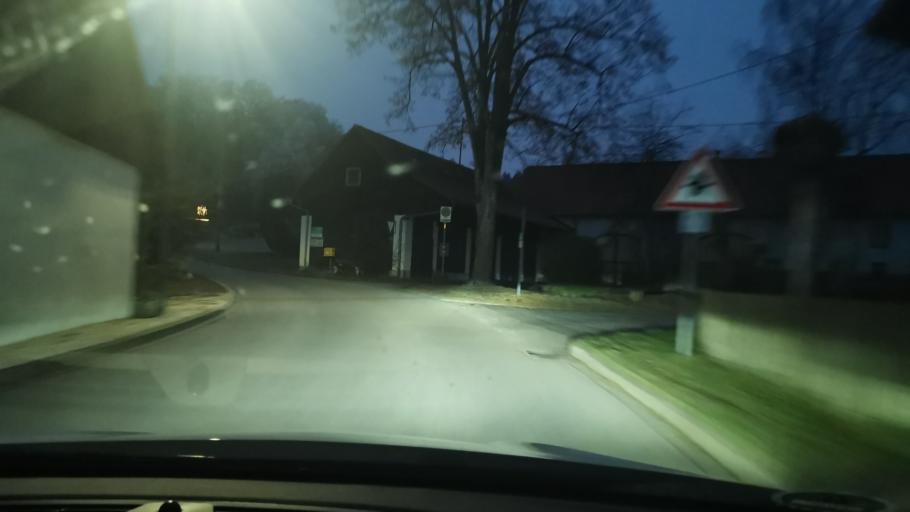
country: DE
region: Bavaria
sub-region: Swabia
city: Petersdorf
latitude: 48.5623
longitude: 11.0268
